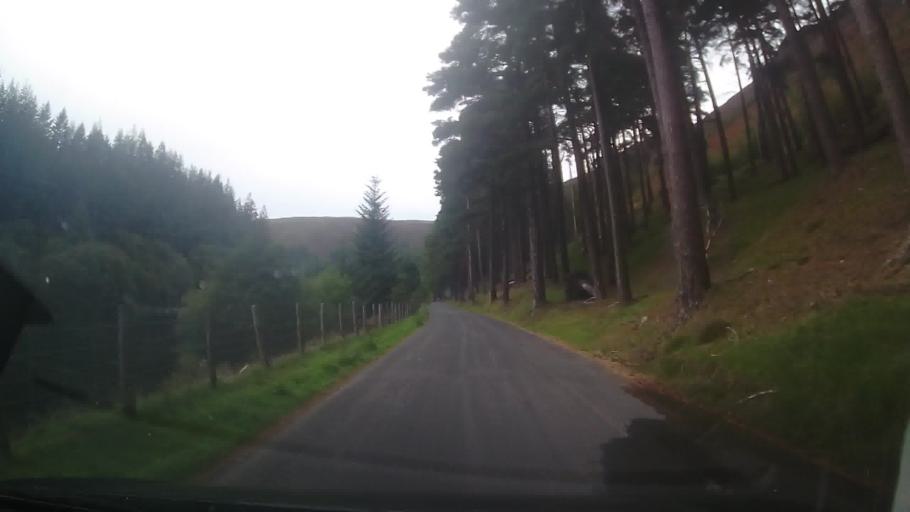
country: GB
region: Wales
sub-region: Sir Powys
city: Rhayader
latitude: 52.2882
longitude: -3.5905
